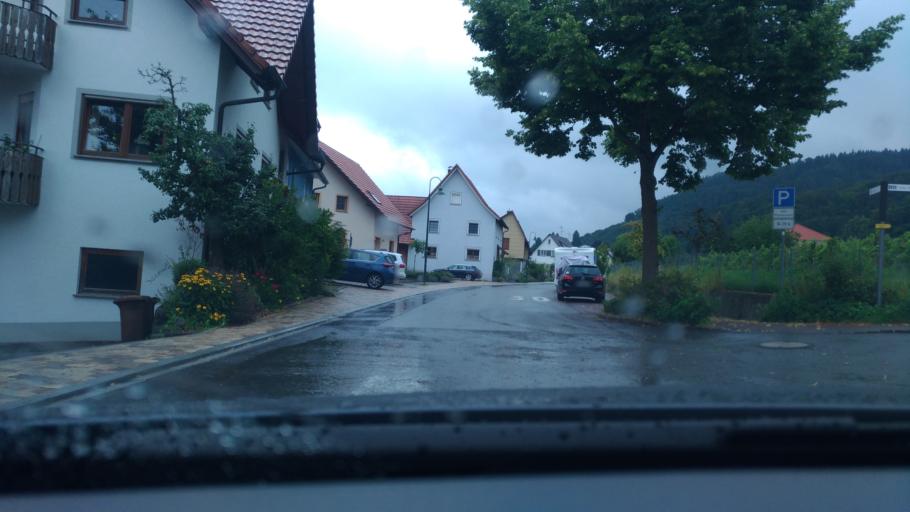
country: DE
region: Baden-Wuerttemberg
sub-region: Freiburg Region
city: Bodman-Ludwigshafen
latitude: 47.7996
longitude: 9.0386
